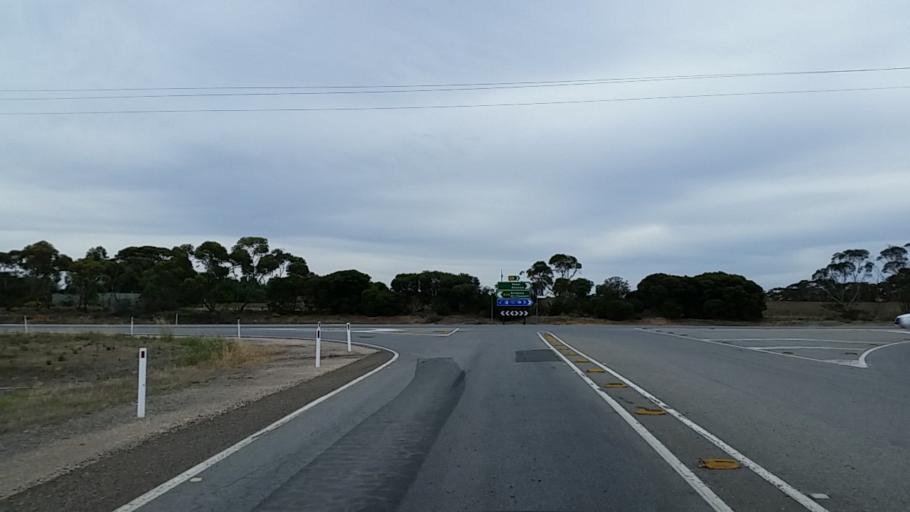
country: AU
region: South Australia
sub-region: Mid Murray
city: Mannum
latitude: -34.9043
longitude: 139.2814
